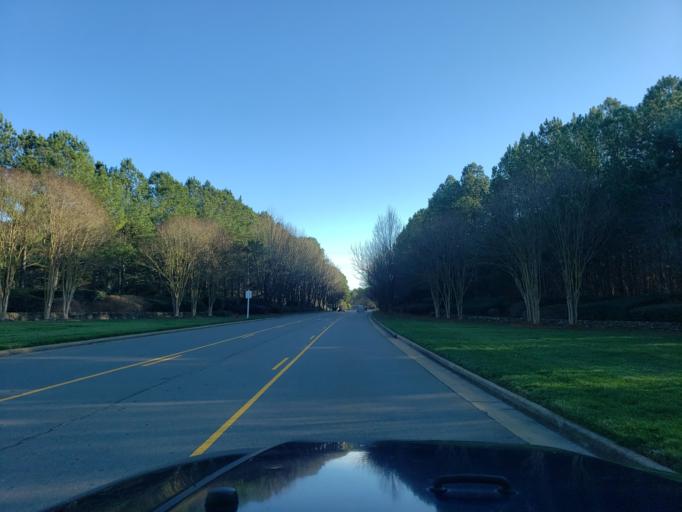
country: US
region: North Carolina
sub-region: Catawba County
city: Lake Norman of Catawba
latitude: 35.5511
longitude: -80.9235
